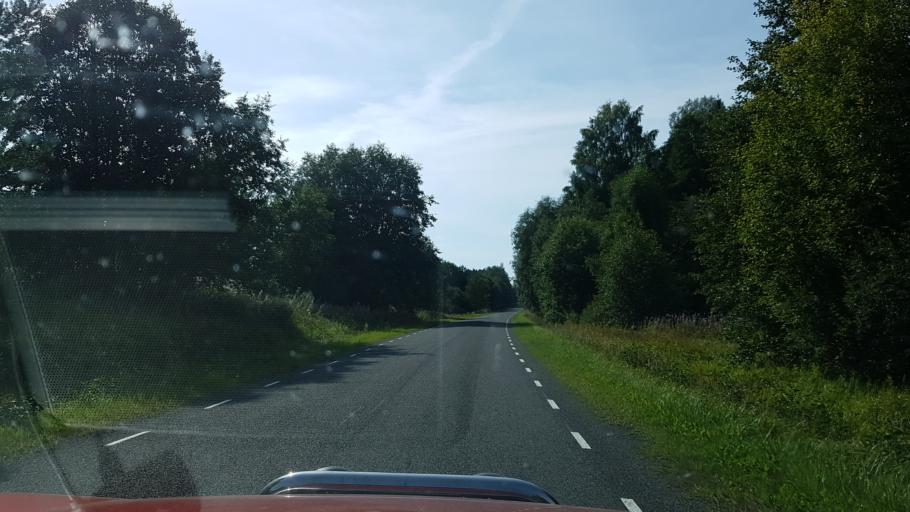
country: EE
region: Viljandimaa
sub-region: Abja vald
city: Abja-Paluoja
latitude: 58.3350
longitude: 25.2242
